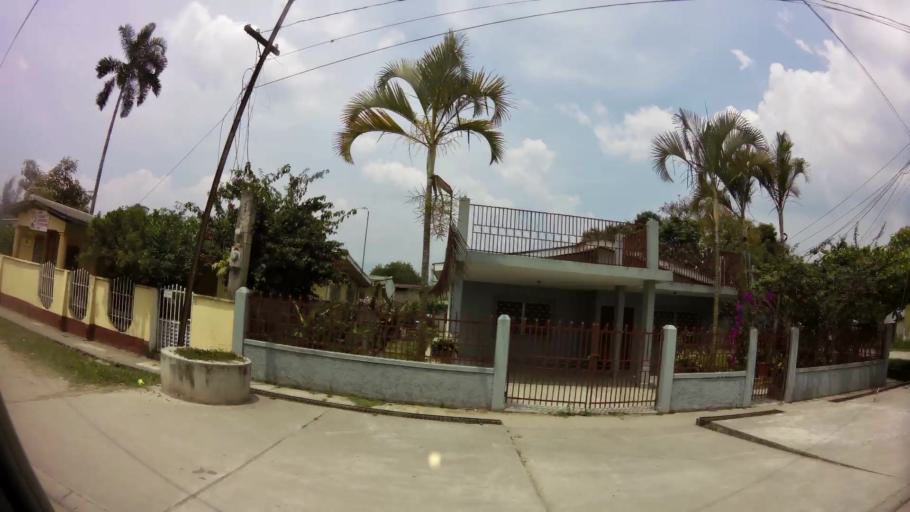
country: HN
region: Comayagua
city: Siguatepeque
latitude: 14.6006
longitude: -87.8368
